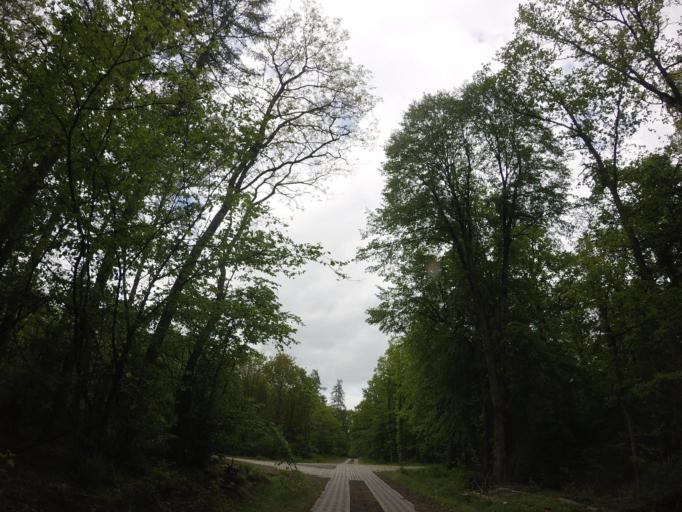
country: PL
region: West Pomeranian Voivodeship
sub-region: Powiat stargardzki
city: Dolice
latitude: 53.2040
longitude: 15.2664
